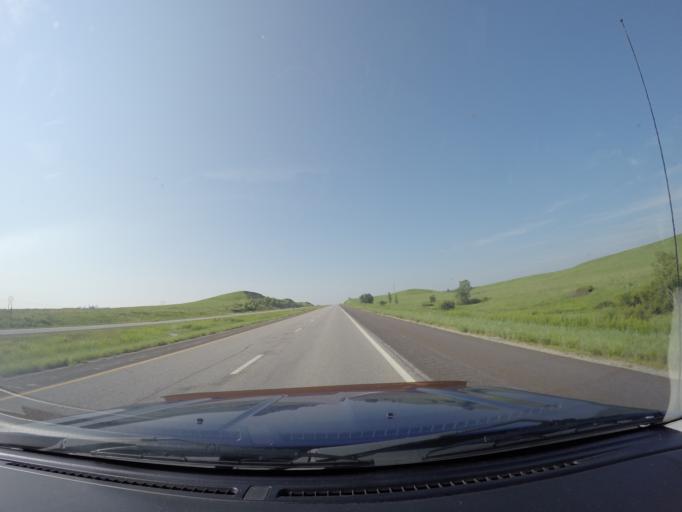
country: US
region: Kansas
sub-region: Riley County
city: Manhattan
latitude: 39.0789
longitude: -96.5385
